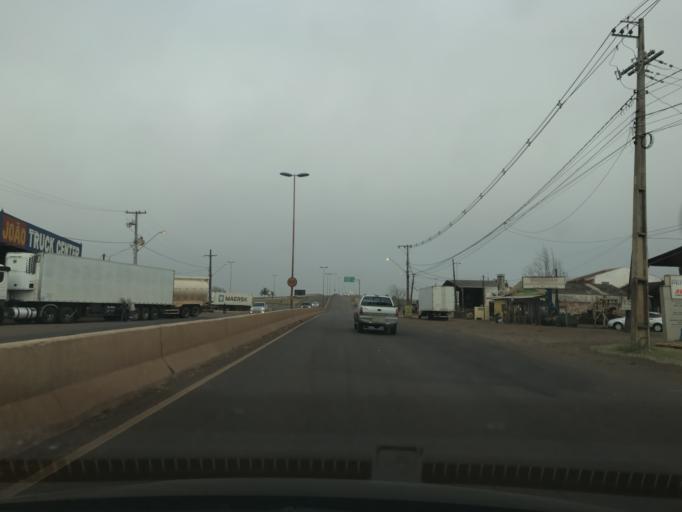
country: BR
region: Parana
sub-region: Toledo
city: Toledo
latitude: -24.7168
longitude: -53.7087
